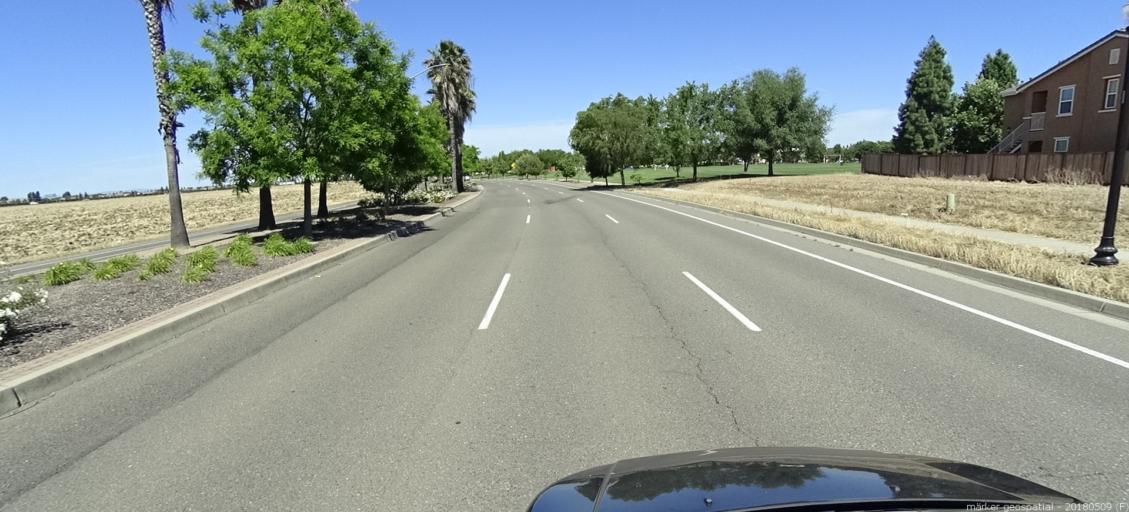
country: US
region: California
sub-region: Yolo County
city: West Sacramento
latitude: 38.6595
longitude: -121.5271
